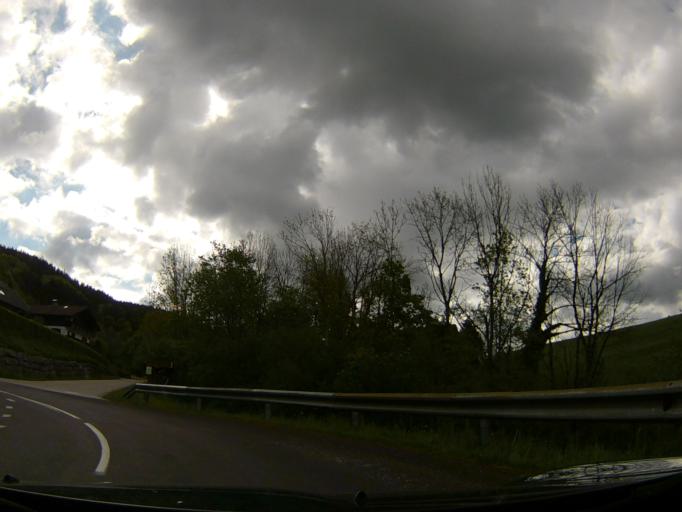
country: AT
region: Upper Austria
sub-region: Politischer Bezirk Vocklabruck
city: Mondsee
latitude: 47.8587
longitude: 13.3598
